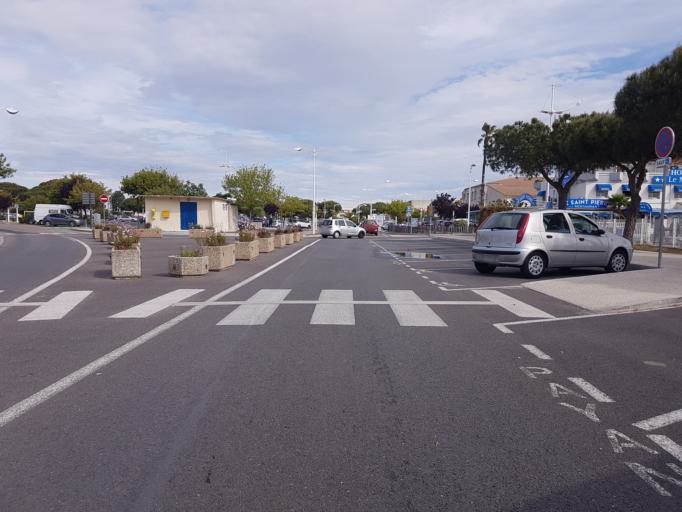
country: FR
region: Languedoc-Roussillon
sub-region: Departement du Gard
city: Le Grau-du-Roi
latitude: 43.5397
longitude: 4.1365
